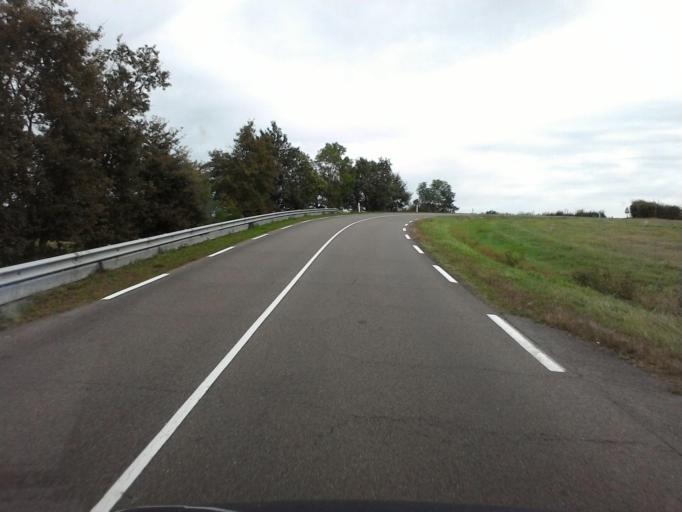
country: FR
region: Bourgogne
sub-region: Departement de Saone-et-Loire
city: Saint-Eusebe
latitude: 46.6487
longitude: 4.4448
